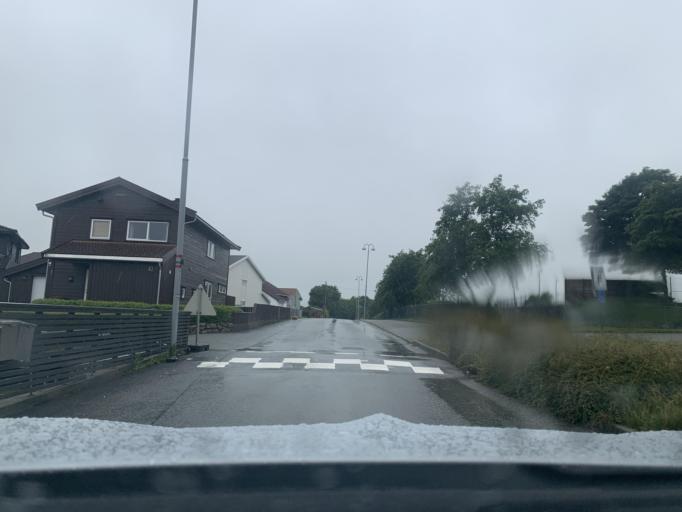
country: NO
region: Rogaland
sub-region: Time
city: Bryne
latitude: 58.7322
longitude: 5.6438
